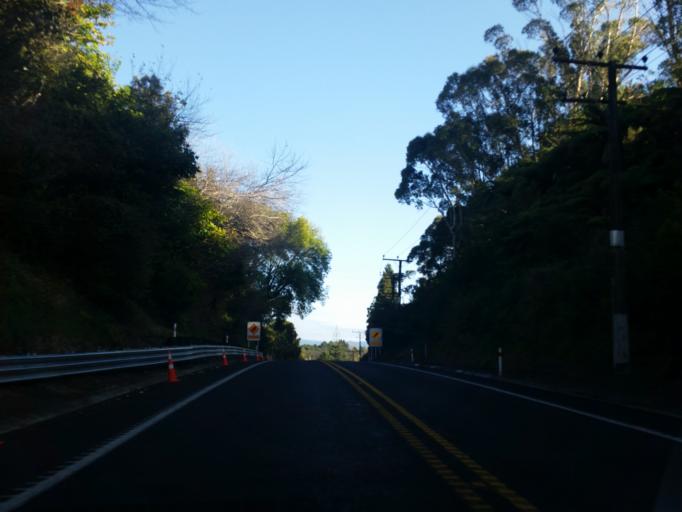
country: NZ
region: Bay of Plenty
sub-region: Western Bay of Plenty District
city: Katikati
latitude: -37.6559
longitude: 175.9990
